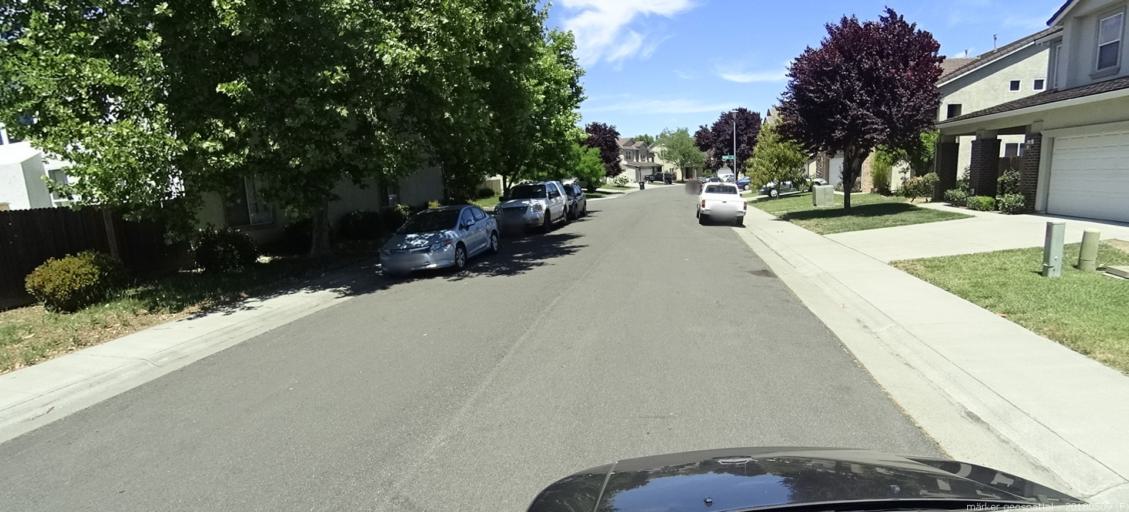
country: US
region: California
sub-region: Sacramento County
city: Sacramento
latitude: 38.6362
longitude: -121.5112
